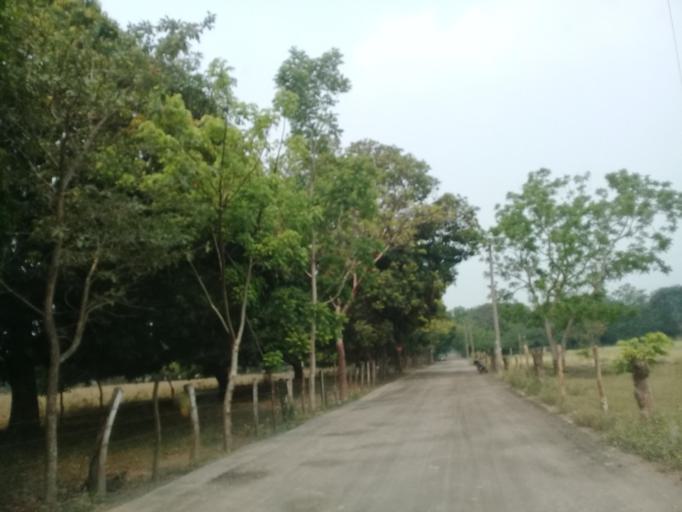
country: MX
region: Veracruz
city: Jamapa
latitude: 18.9521
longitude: -96.1979
